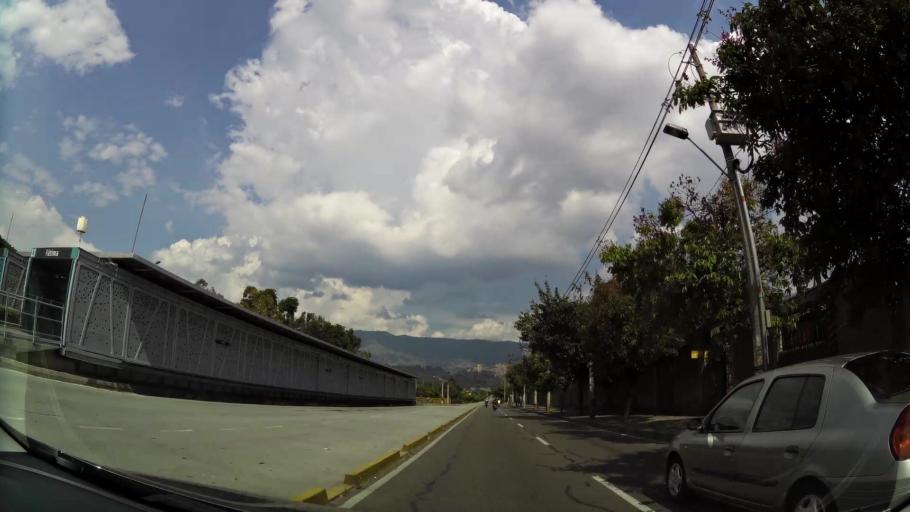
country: CO
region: Antioquia
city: Medellin
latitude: 6.2316
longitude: -75.5869
